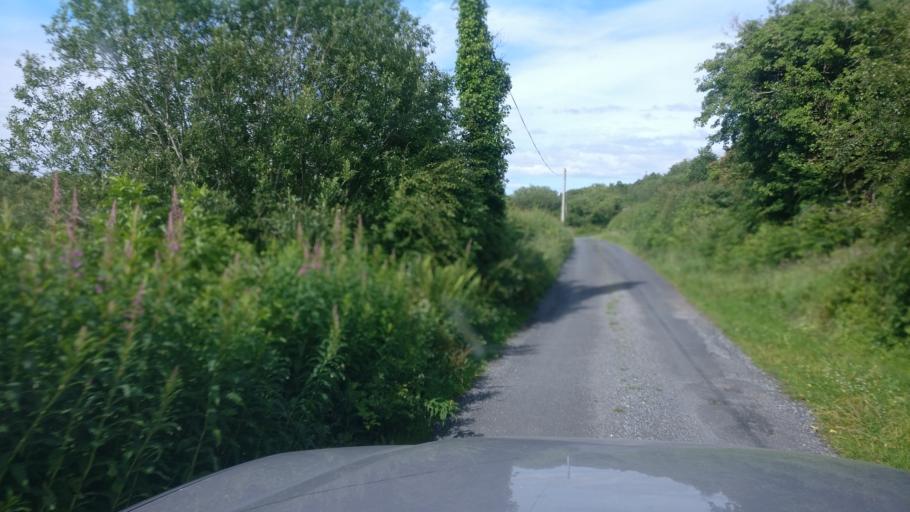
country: IE
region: Connaught
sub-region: County Galway
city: Gort
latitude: 53.0965
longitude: -8.6973
